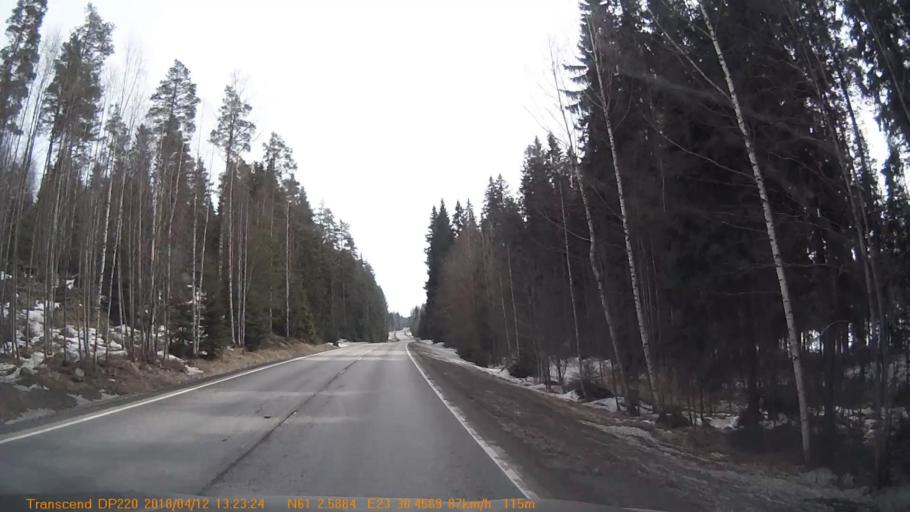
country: FI
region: Pirkanmaa
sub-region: Etelae-Pirkanmaa
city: Urjala
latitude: 61.0421
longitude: 23.6426
